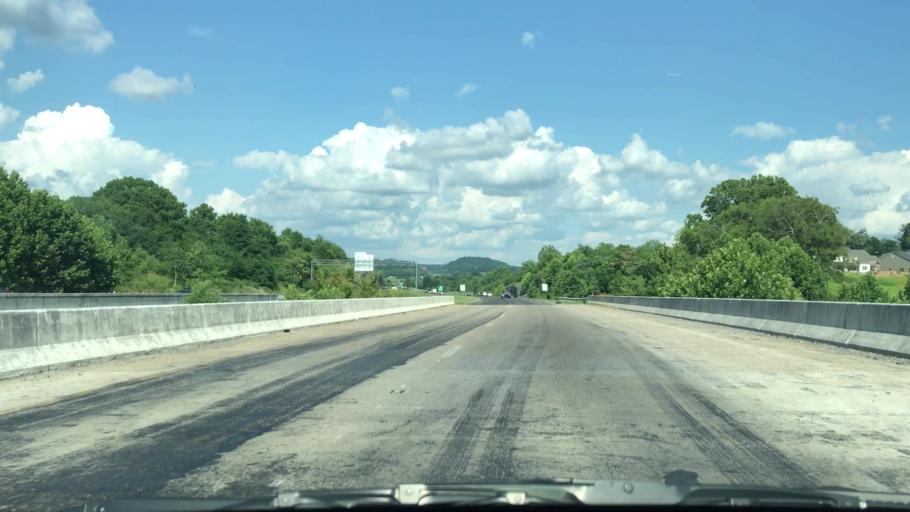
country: US
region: Tennessee
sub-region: Williamson County
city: Thompson's Station
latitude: 35.8209
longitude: -86.8759
